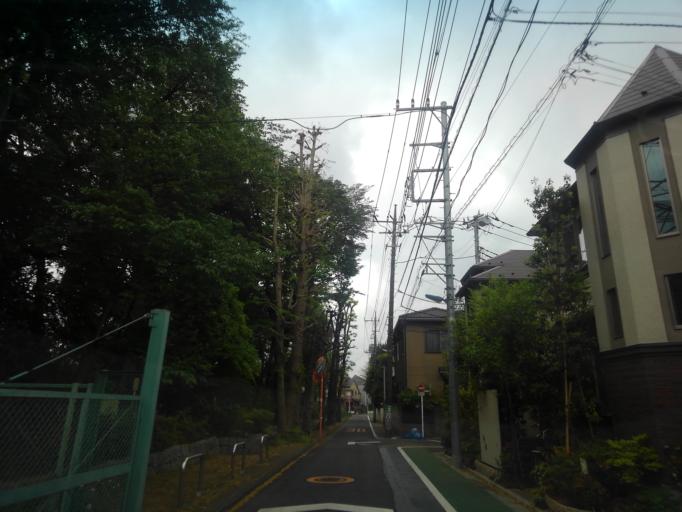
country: JP
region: Tokyo
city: Musashino
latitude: 35.7197
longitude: 139.5863
